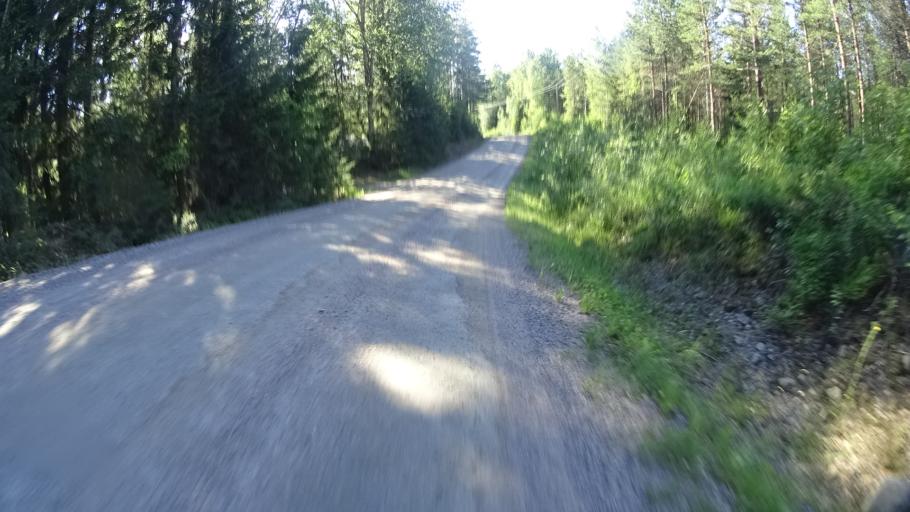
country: FI
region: Uusimaa
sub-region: Helsinki
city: Karkkila
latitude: 60.6475
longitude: 24.1391
